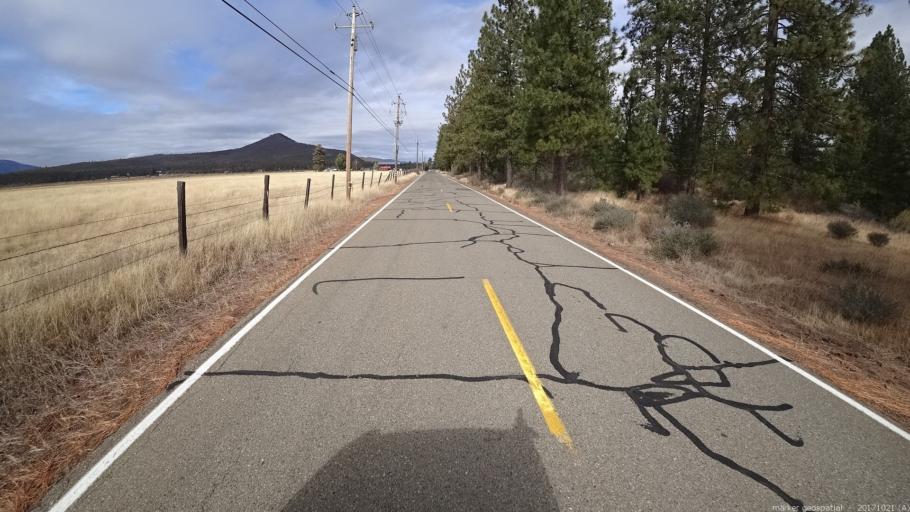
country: US
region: California
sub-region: Shasta County
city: Burney
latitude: 40.9127
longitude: -121.6469
